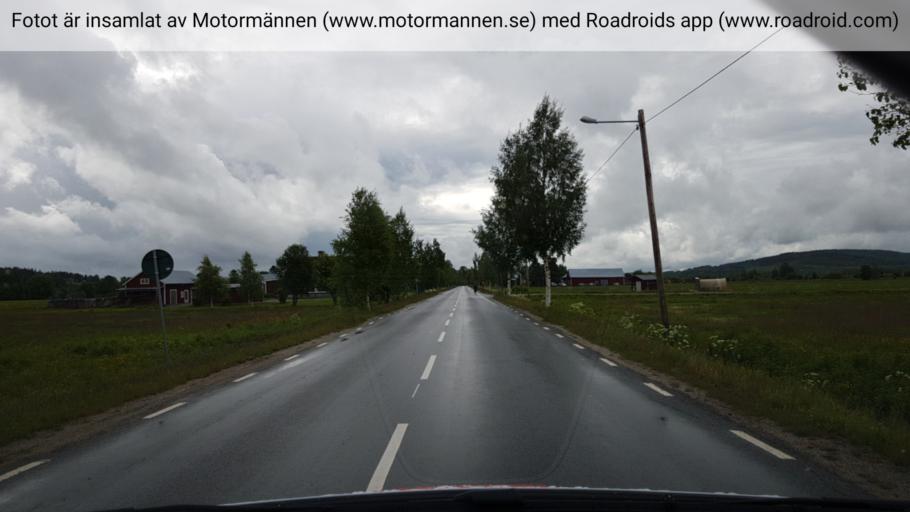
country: SE
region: Vaesterbotten
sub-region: Vannas Kommun
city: Vannasby
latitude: 63.9063
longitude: 19.8610
